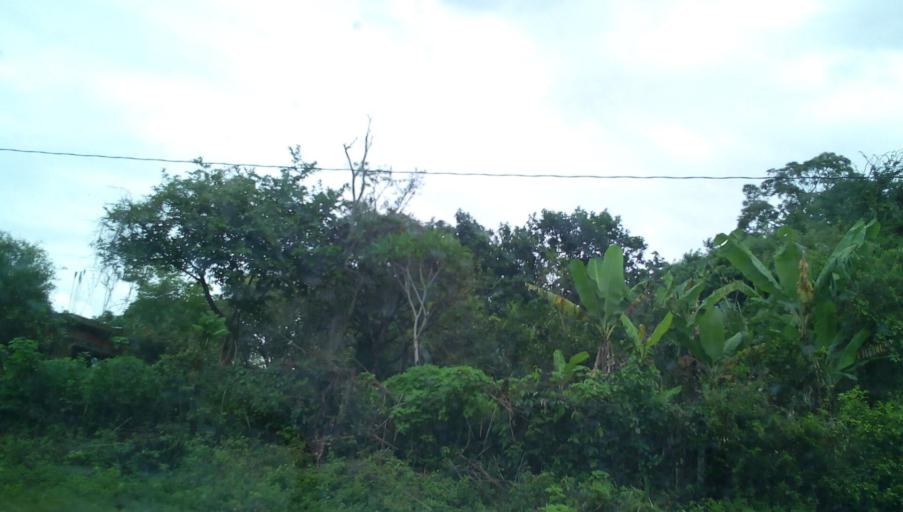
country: MX
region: Veracruz
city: Tepetzintla
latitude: 21.1267
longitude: -97.8533
